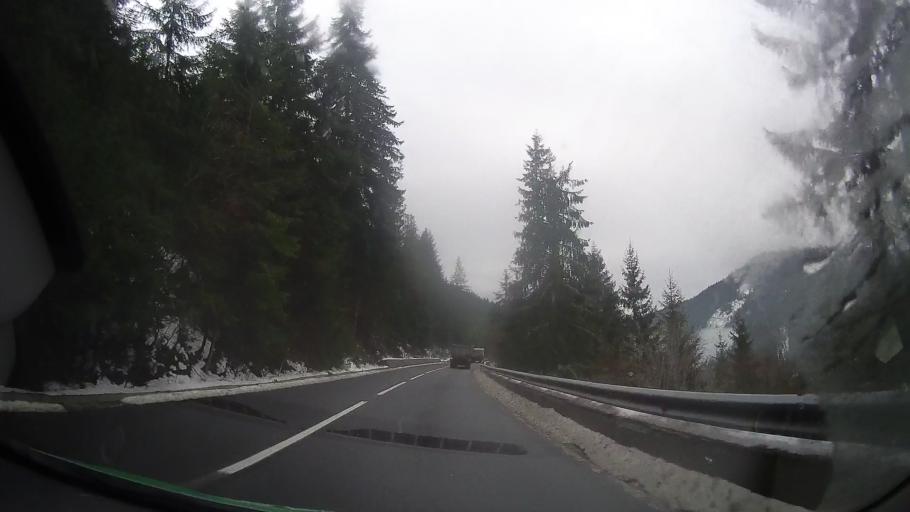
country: RO
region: Harghita
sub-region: Municipiul Gheorgheni
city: Gheorgheni
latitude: 46.7717
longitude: 25.7114
